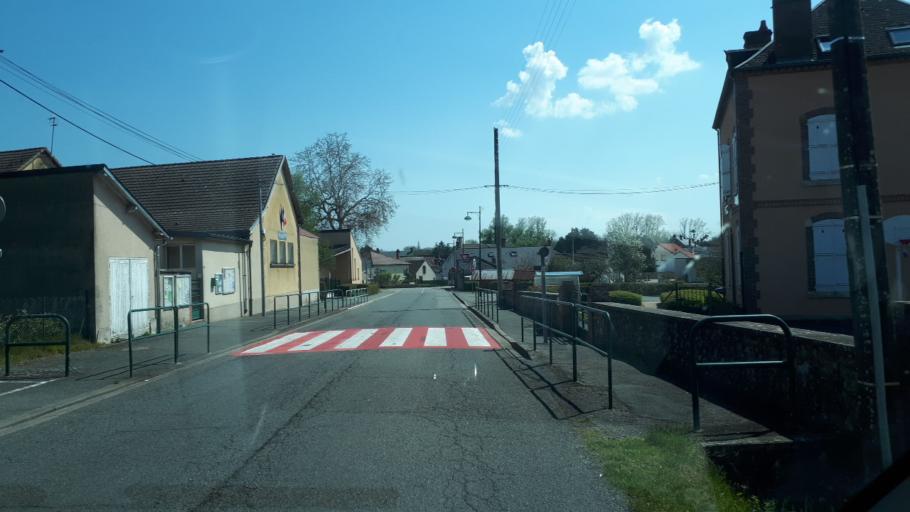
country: FR
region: Centre
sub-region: Departement du Cher
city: Neuvy-sur-Barangeon
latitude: 47.3160
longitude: 2.2514
